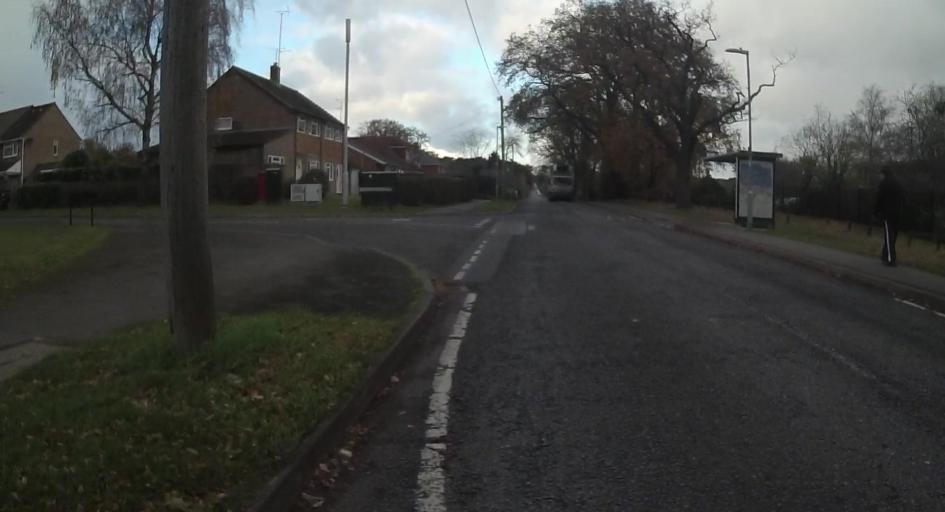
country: GB
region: England
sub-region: Bracknell Forest
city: Sandhurst
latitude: 51.3505
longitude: -0.7825
